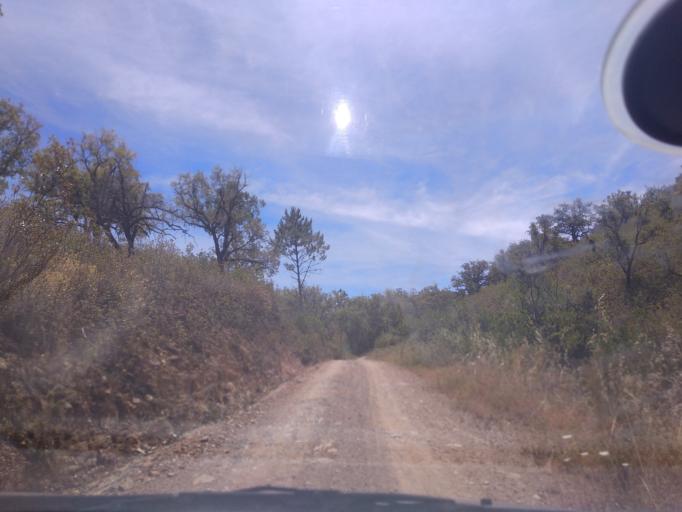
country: PT
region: Faro
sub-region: Sao Bras de Alportel
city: Sao Bras de Alportel
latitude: 37.2100
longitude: -7.8186
